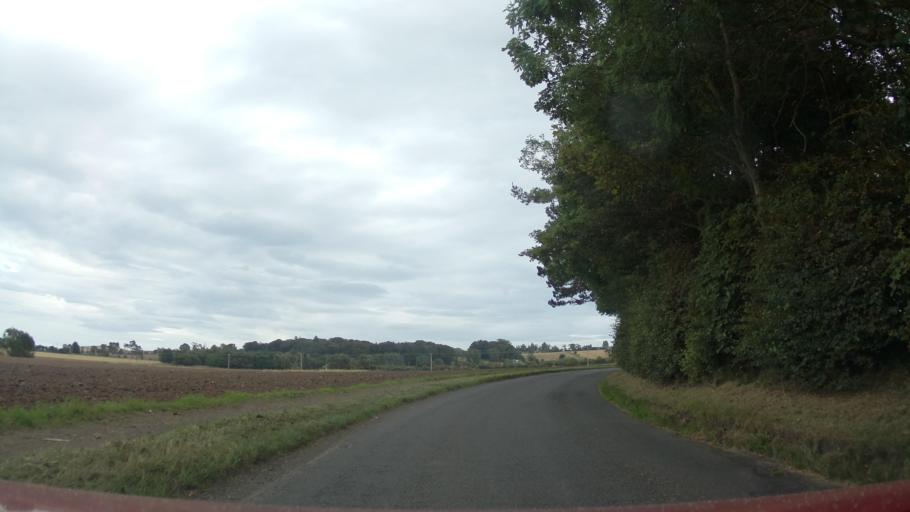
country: GB
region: Scotland
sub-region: Fife
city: Saint Andrews
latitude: 56.3281
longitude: -2.7822
